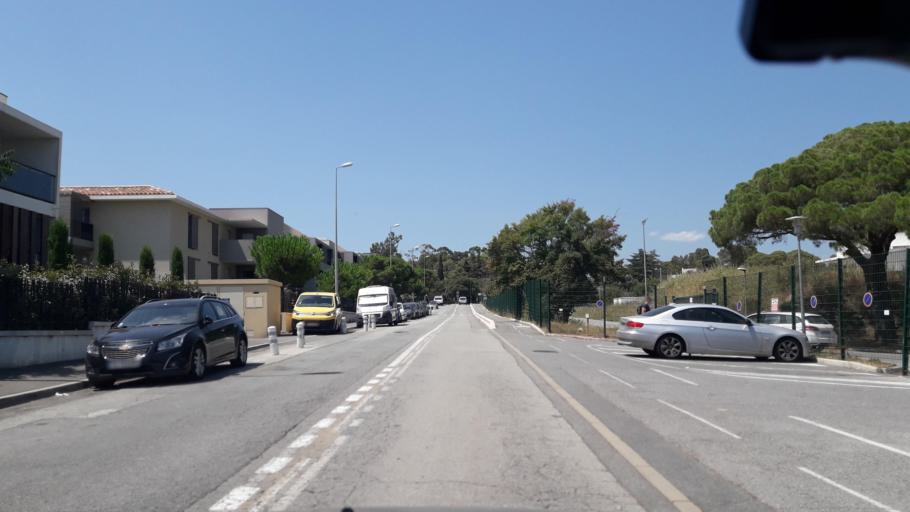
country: FR
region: Provence-Alpes-Cote d'Azur
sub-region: Departement du Var
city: Frejus
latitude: 43.4461
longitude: 6.7540
